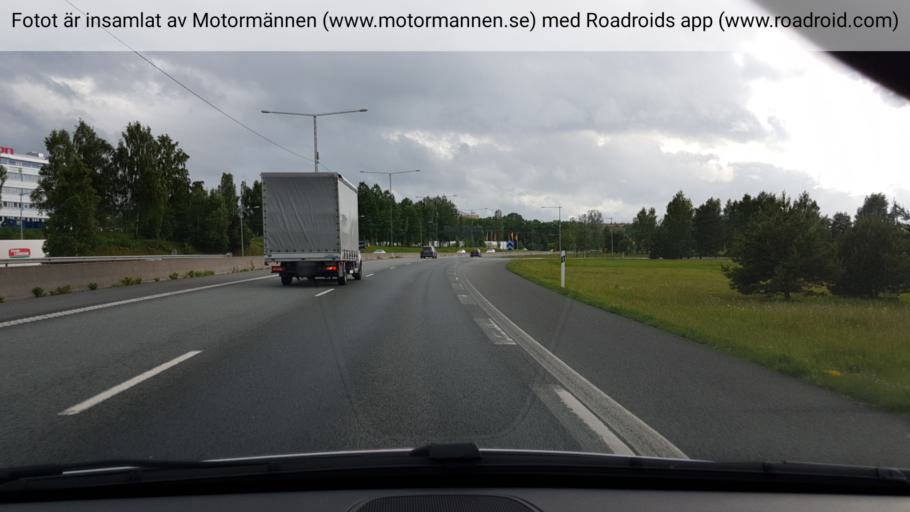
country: SE
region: Joenkoeping
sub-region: Jonkopings Kommun
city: Huskvarna
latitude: 57.7888
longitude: 14.2614
